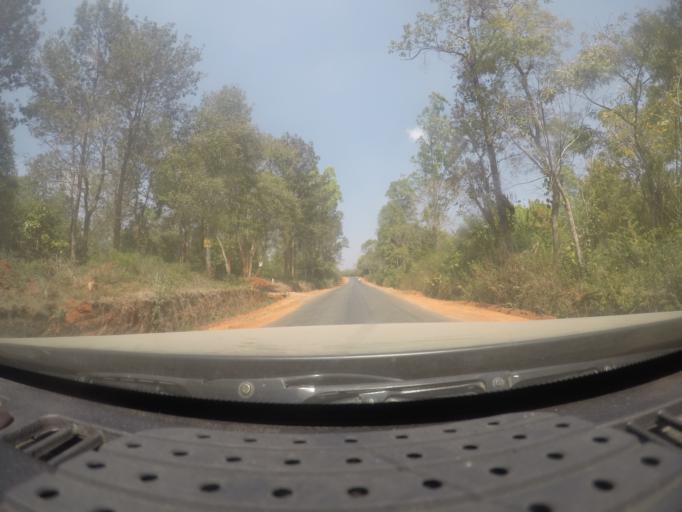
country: MM
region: Shan
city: Taunggyi
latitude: 21.0064
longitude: 96.5258
